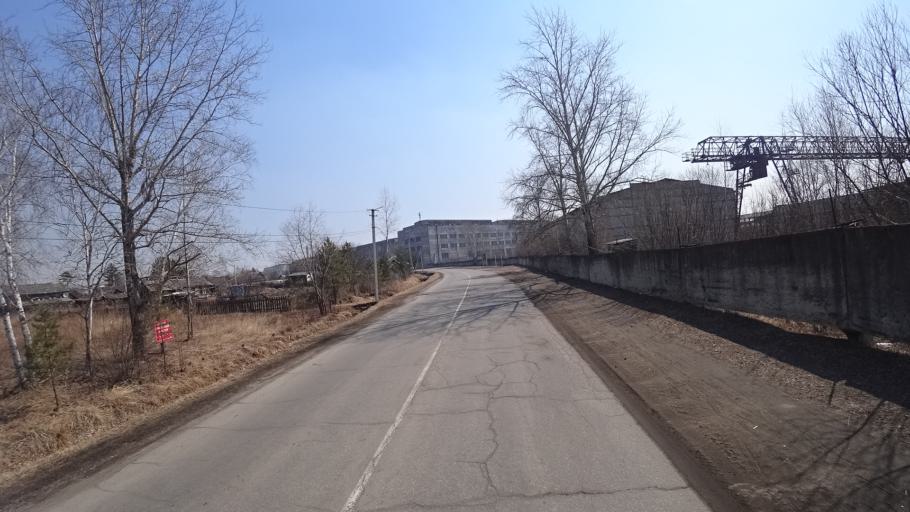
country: RU
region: Amur
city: Novobureyskiy
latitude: 49.7931
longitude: 129.8558
